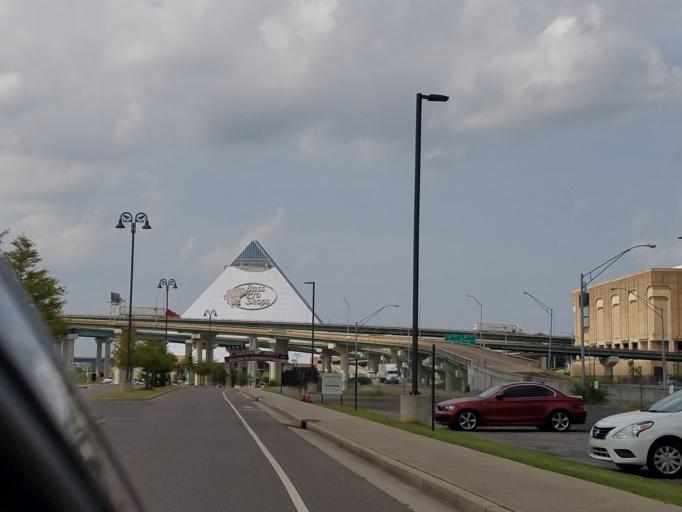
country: US
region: Tennessee
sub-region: Shelby County
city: Memphis
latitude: 35.1501
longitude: -90.0525
